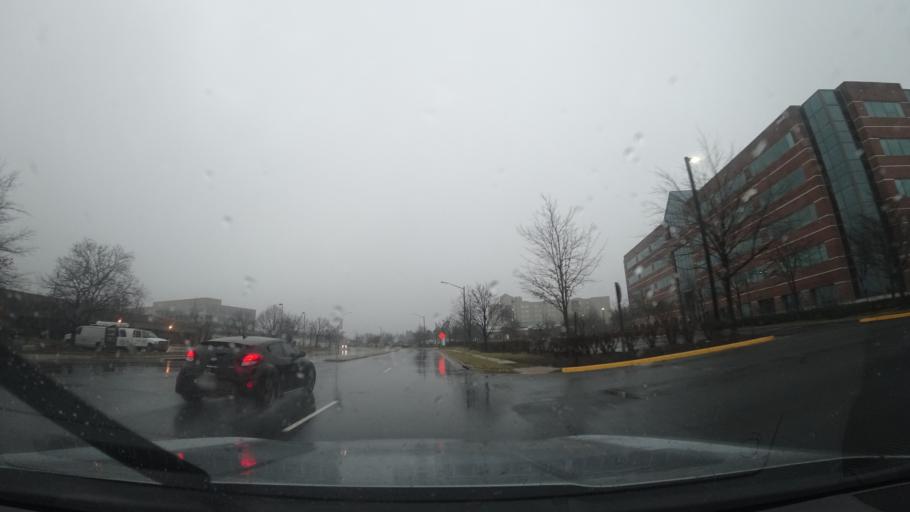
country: US
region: Virginia
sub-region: Fairfax County
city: Floris
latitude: 38.9562
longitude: -77.4123
